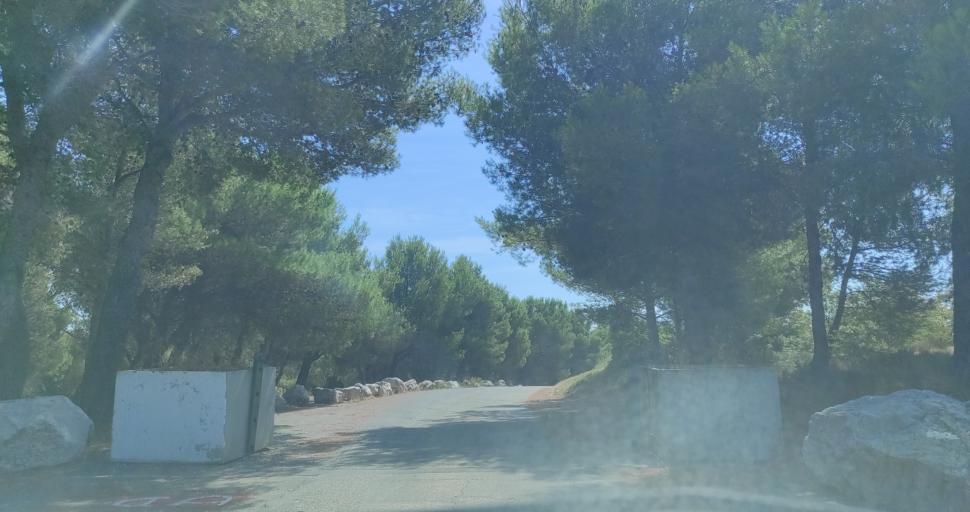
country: FR
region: Provence-Alpes-Cote d'Azur
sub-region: Departement des Bouches-du-Rhone
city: Martigues
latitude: 43.4176
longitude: 5.0427
